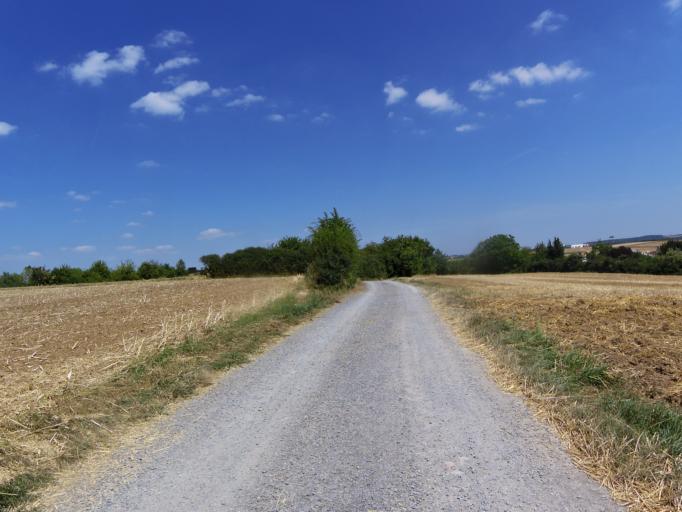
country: DE
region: Bavaria
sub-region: Regierungsbezirk Unterfranken
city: Wuerzburg
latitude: 49.8168
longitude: 9.9574
